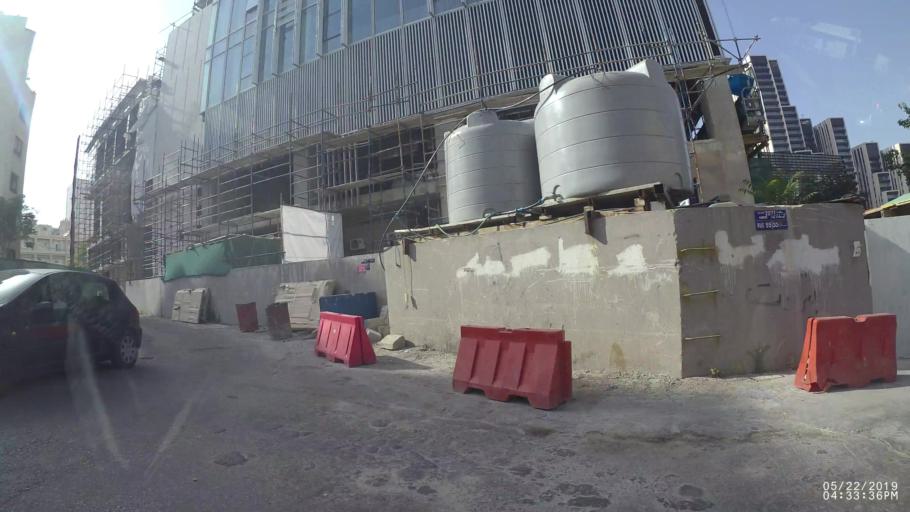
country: LB
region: Beyrouth
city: Beirut
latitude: 33.8972
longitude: 35.4955
